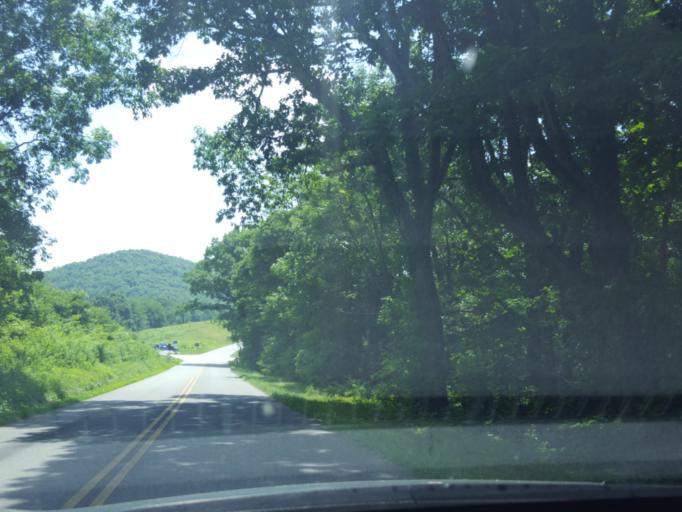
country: US
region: Virginia
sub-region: Nelson County
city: Nellysford
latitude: 37.9035
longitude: -78.9845
